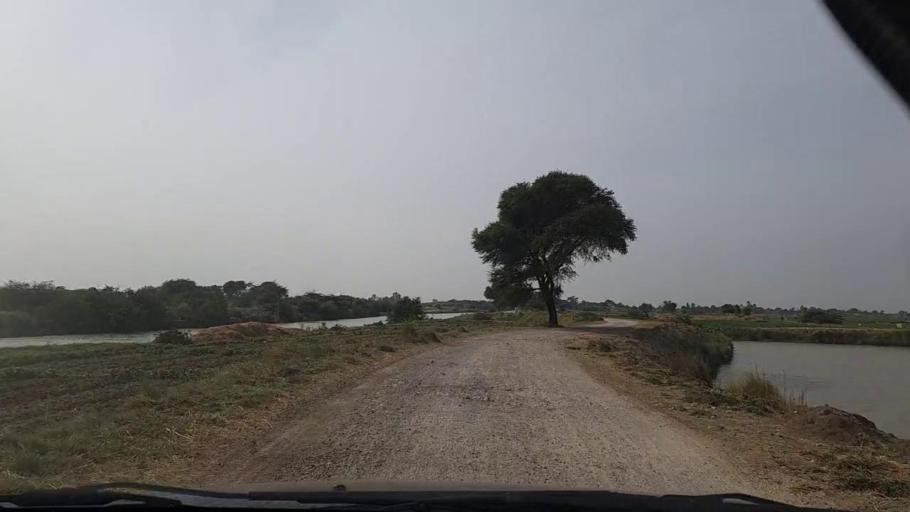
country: PK
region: Sindh
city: Thatta
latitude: 24.5695
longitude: 67.8699
